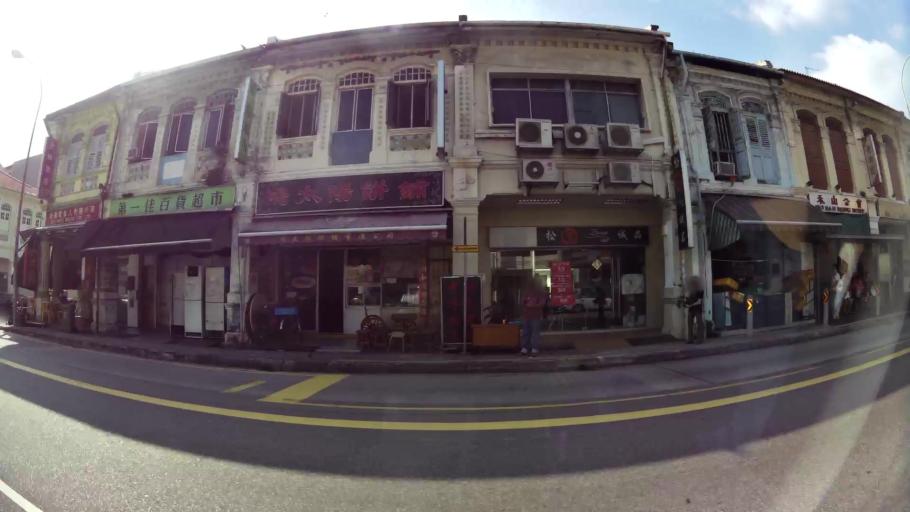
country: SG
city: Singapore
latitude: 1.3141
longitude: 103.8873
